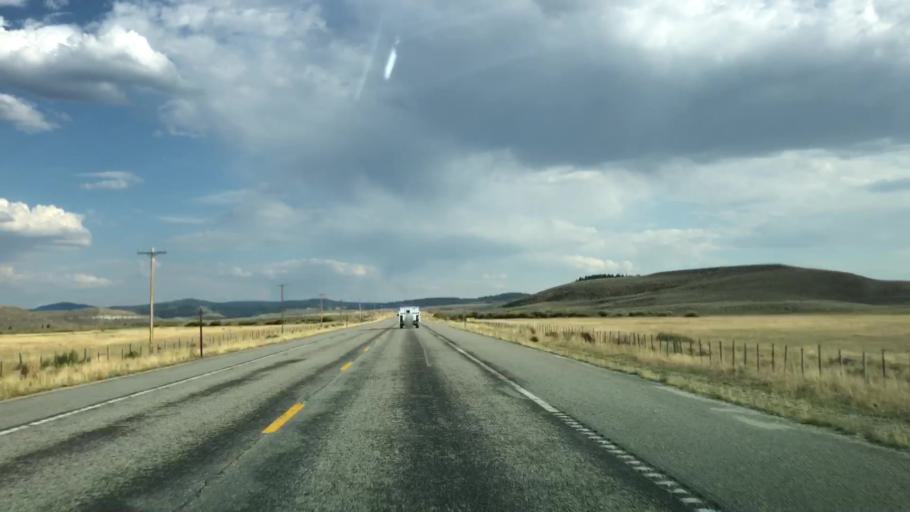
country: US
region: Wyoming
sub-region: Teton County
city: Hoback
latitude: 43.1856
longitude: -110.3925
